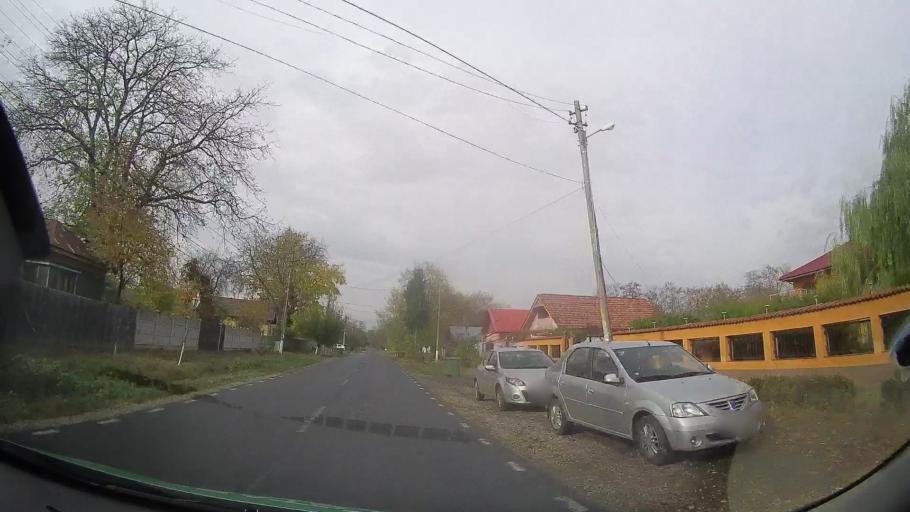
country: RO
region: Ialomita
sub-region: Comuna Fierbinti-Targ
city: Fierbinti-Targ
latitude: 44.7043
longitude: 26.3256
